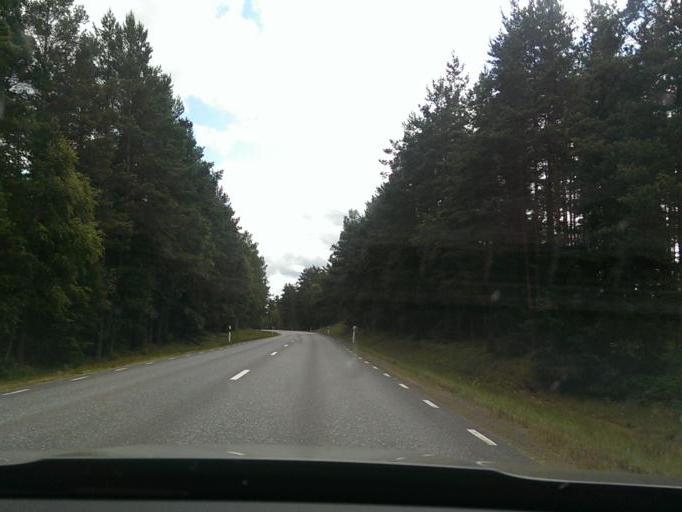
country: SE
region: Joenkoeping
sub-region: Gnosjo Kommun
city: Hillerstorp
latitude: 57.2964
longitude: 13.9311
